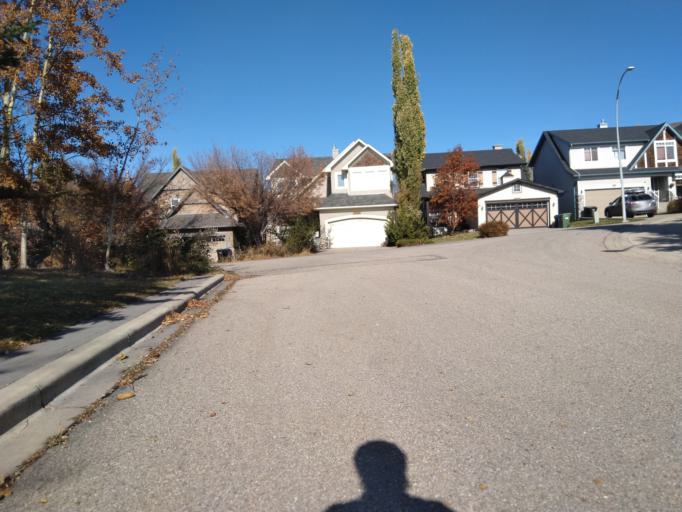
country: CA
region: Alberta
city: Calgary
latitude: 51.1597
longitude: -114.0994
